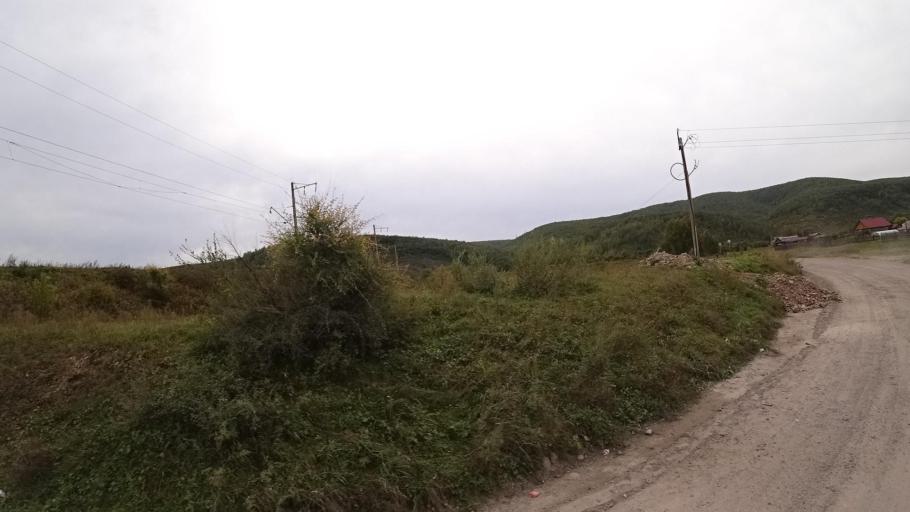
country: RU
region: Jewish Autonomous Oblast
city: Khingansk
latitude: 49.0305
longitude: 131.0506
